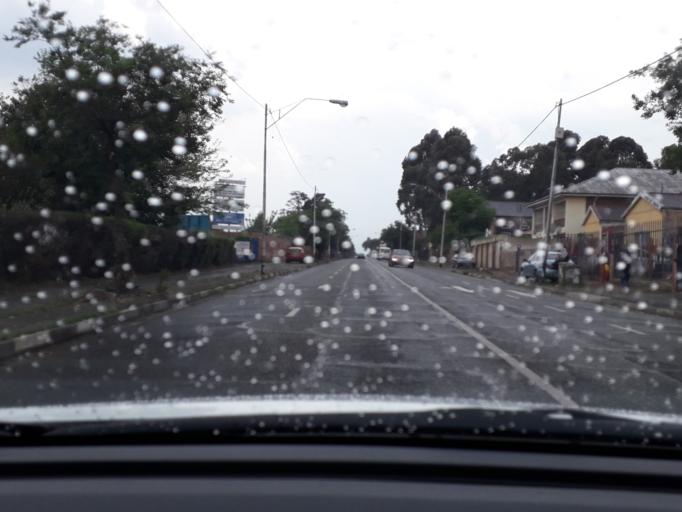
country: ZA
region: Gauteng
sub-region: City of Johannesburg Metropolitan Municipality
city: Johannesburg
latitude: -26.2394
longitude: 28.0349
